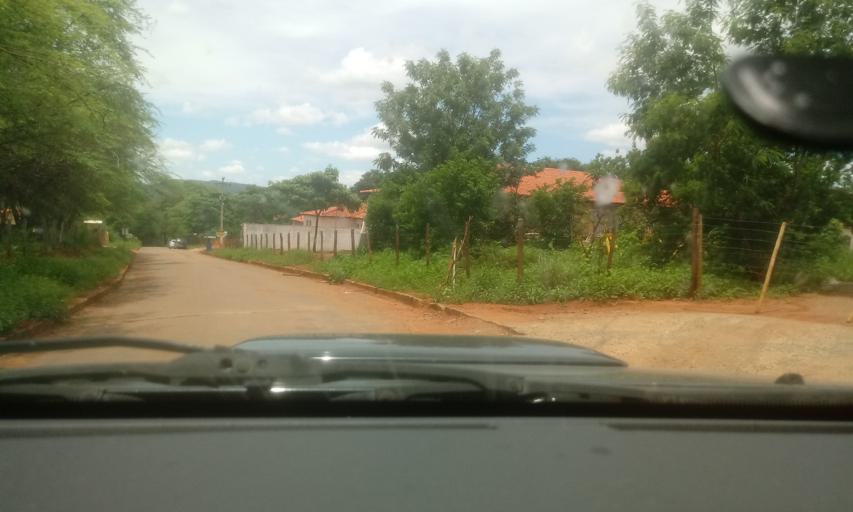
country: BR
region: Bahia
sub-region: Riacho De Santana
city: Riacho de Santana
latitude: -13.6008
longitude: -42.9455
